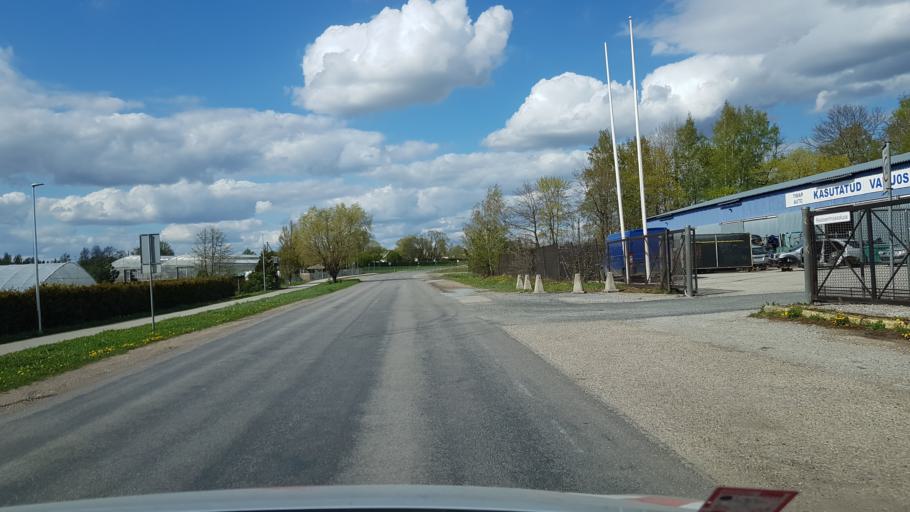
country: EE
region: Tartu
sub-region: Tartu linn
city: Tartu
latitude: 58.3673
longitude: 26.7985
